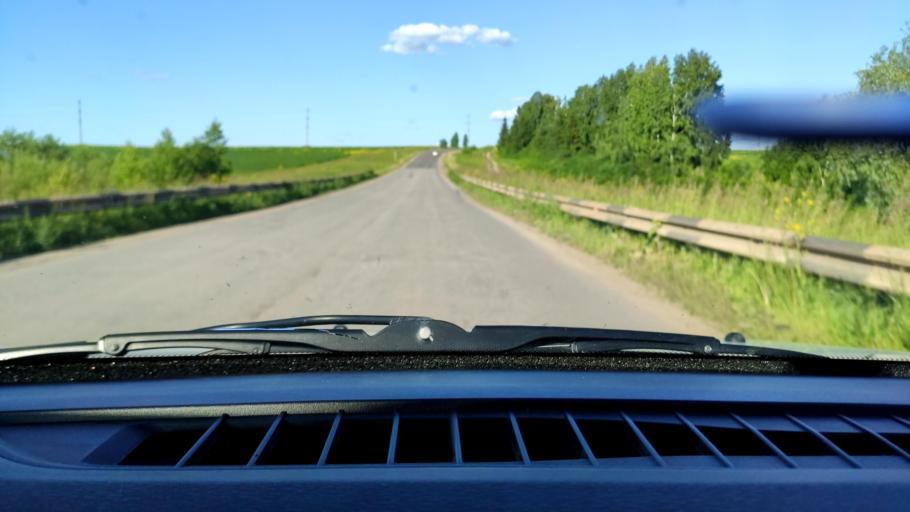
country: RU
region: Perm
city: Orda
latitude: 57.1895
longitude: 56.8563
